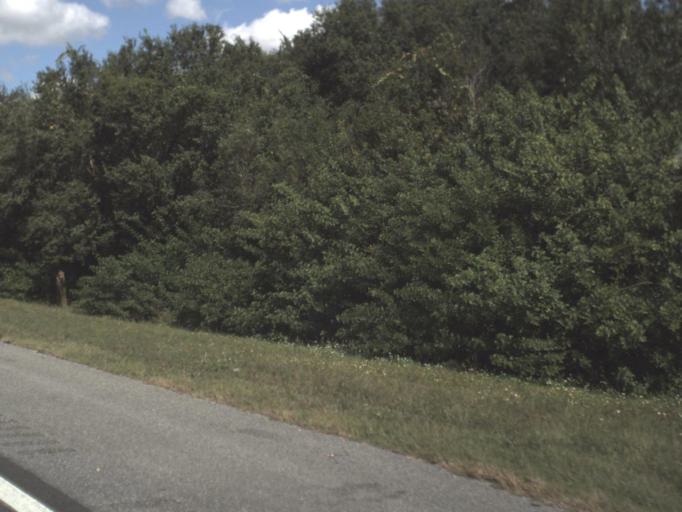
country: US
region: Florida
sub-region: Osceola County
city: Buenaventura Lakes
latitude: 28.3021
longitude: -81.3600
